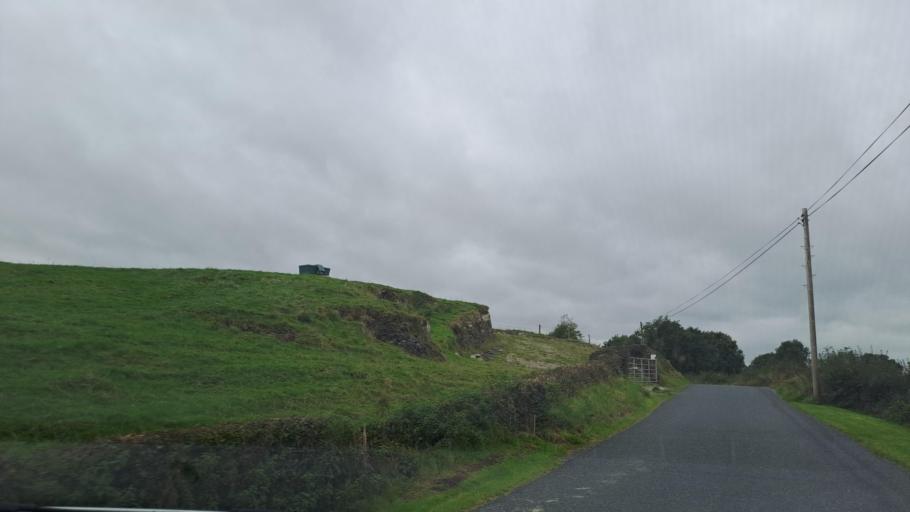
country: IE
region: Ulster
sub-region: An Cabhan
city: Kingscourt
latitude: 54.0109
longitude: -6.8803
